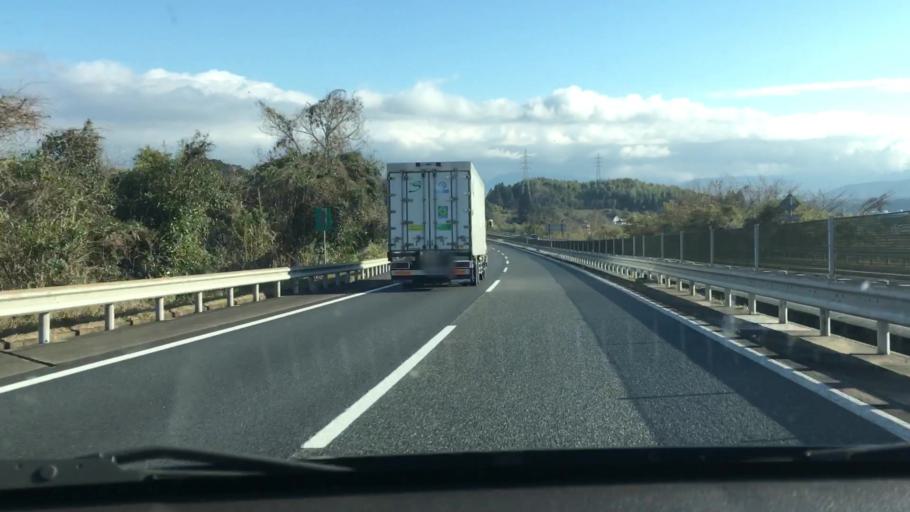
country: JP
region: Kumamoto
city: Hitoyoshi
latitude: 32.2378
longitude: 130.7621
